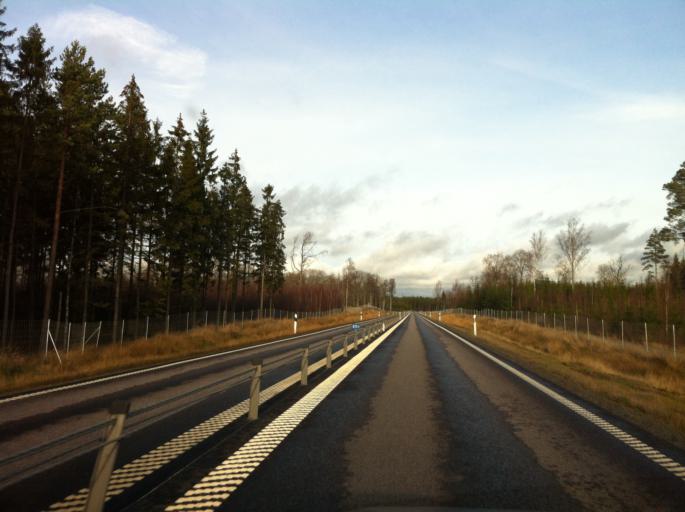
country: SE
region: Kronoberg
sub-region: Almhults Kommun
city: AElmhult
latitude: 56.6388
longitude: 14.2655
